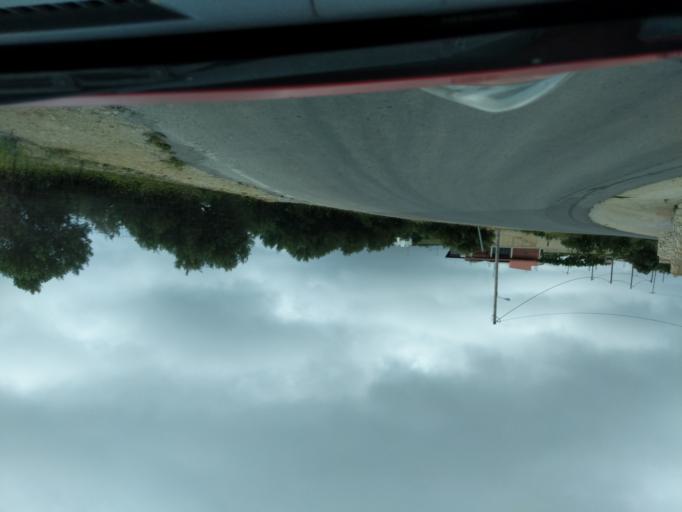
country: GR
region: Crete
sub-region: Nomos Chanias
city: Platanos
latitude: 35.4770
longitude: 23.5921
